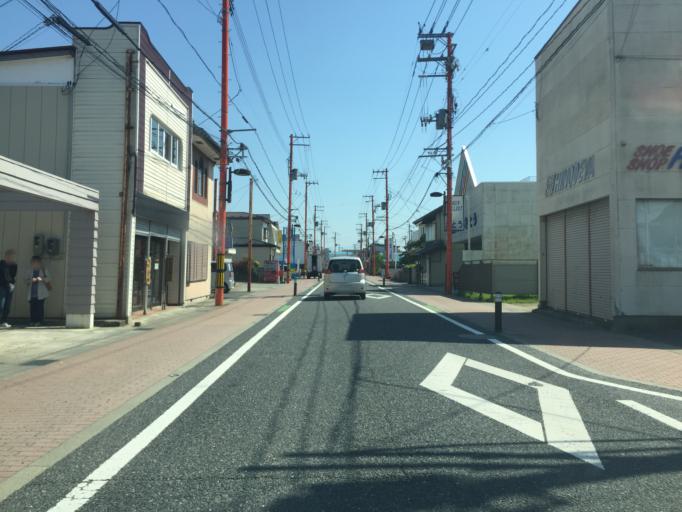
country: JP
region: Miyagi
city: Matsushima
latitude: 38.3853
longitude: 141.0699
